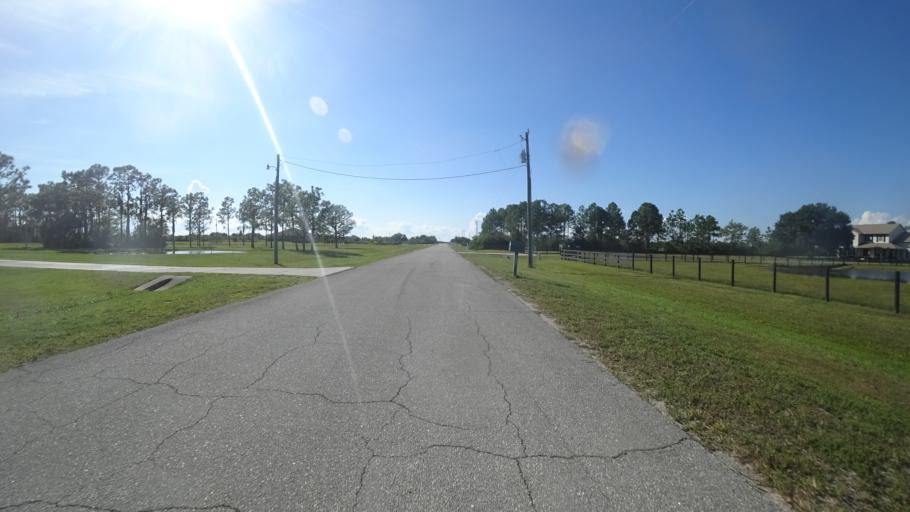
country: US
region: Florida
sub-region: Sarasota County
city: The Meadows
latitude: 27.4232
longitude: -82.2776
